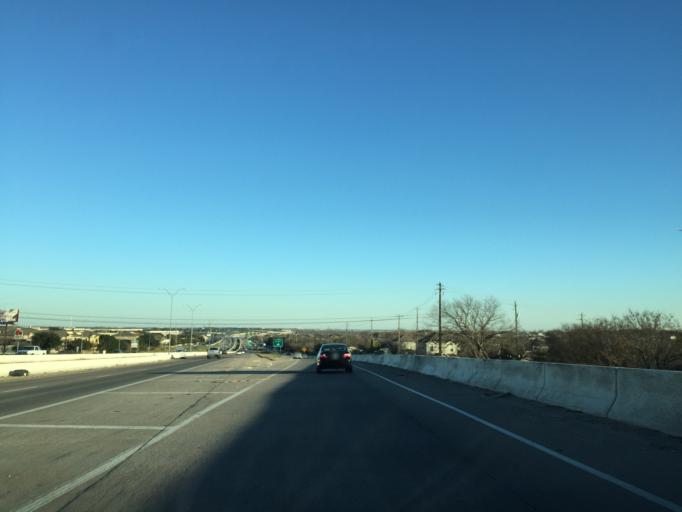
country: US
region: Texas
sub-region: Travis County
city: Austin
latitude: 30.3373
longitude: -97.6969
